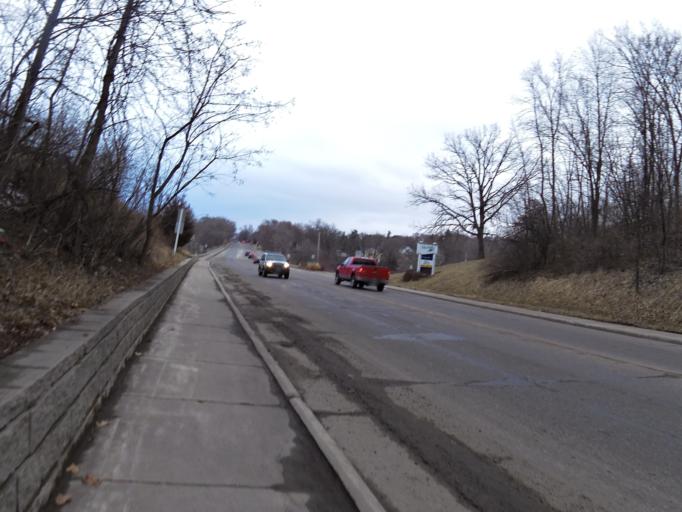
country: US
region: Wisconsin
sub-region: Saint Croix County
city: North Hudson
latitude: 44.9873
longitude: -92.7575
